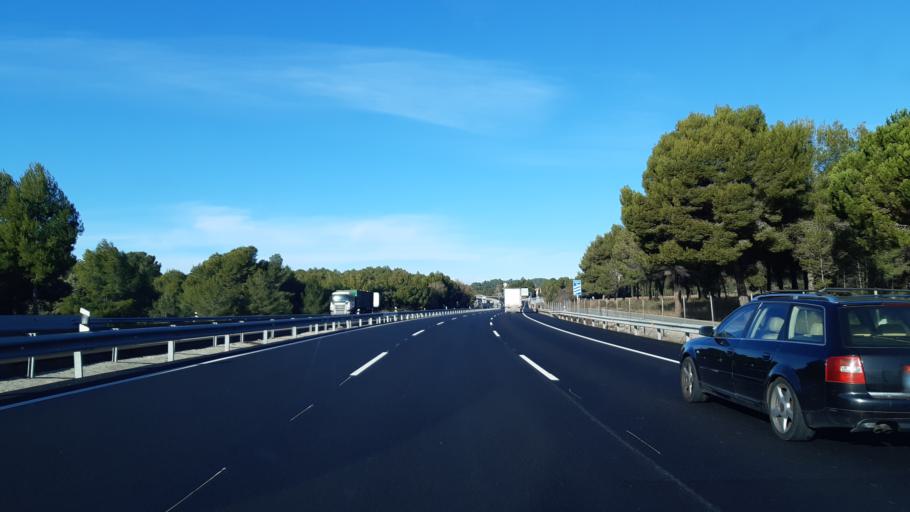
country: ES
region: Catalonia
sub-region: Provincia de Barcelona
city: Collbato
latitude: 41.5694
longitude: 1.7971
